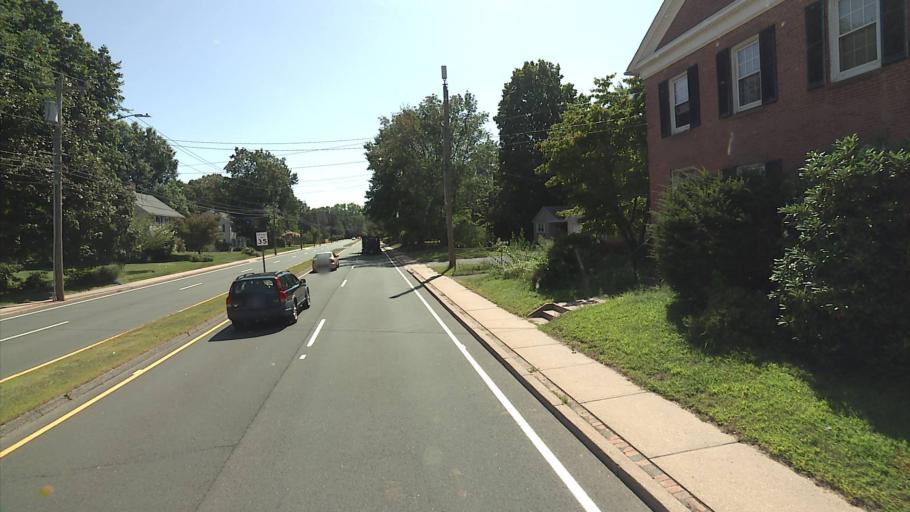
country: US
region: Connecticut
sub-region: Hartford County
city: Windsor
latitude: 41.8348
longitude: -72.6540
